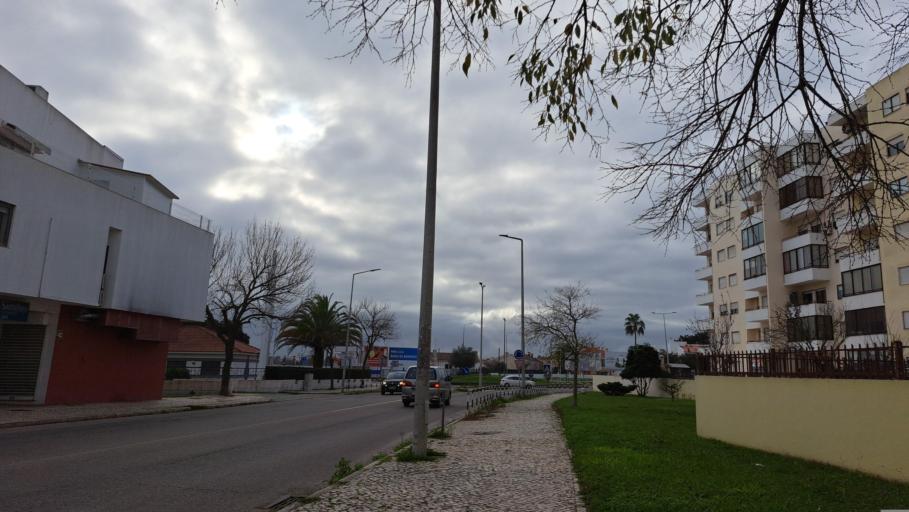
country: PT
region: Setubal
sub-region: Moita
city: Alhos Vedros
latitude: 38.6494
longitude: -9.0467
